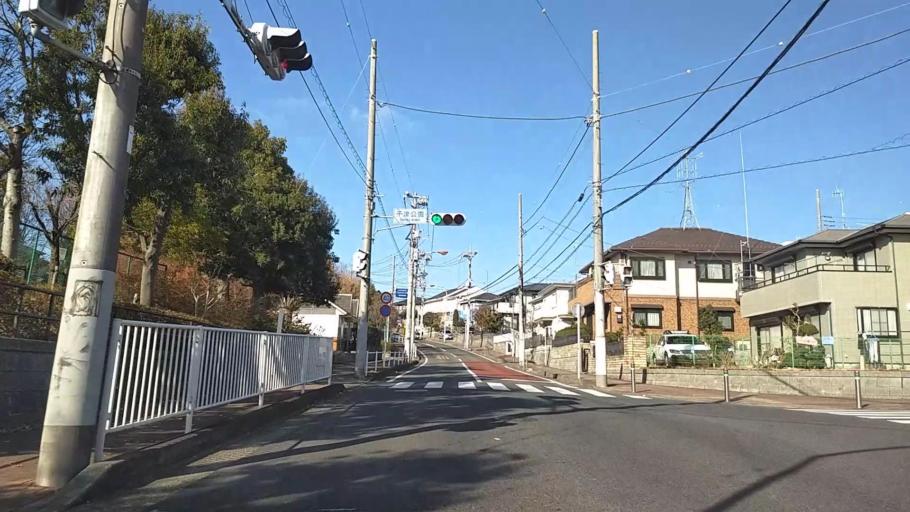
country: JP
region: Kanagawa
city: Isehara
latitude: 35.3942
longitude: 139.3091
